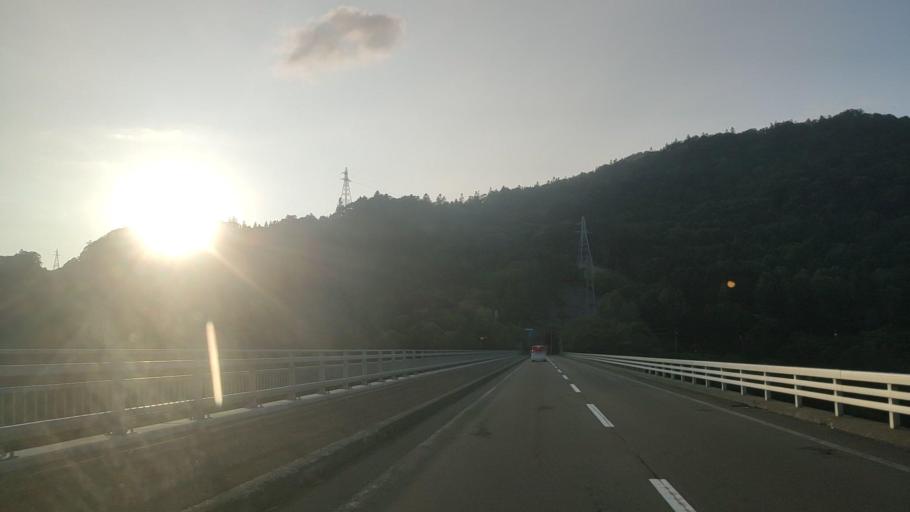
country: JP
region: Hokkaido
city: Bibai
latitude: 43.2441
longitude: 142.0215
